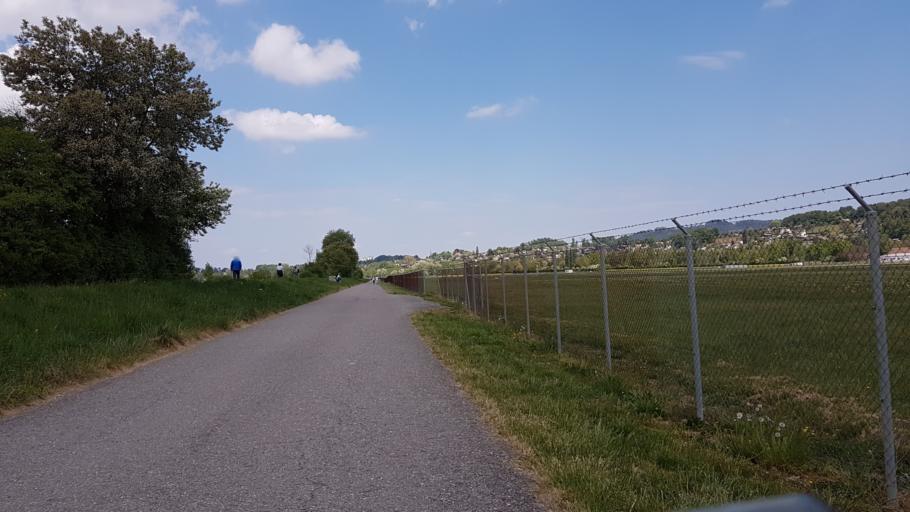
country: CH
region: Bern
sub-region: Bern-Mittelland District
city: Belp
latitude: 46.9094
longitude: 7.4957
